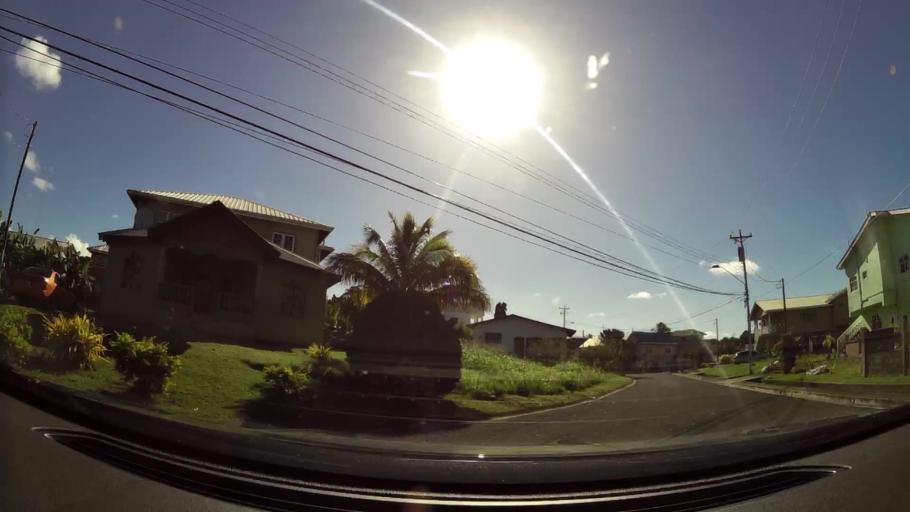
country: TT
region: Tobago
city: Scarborough
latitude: 11.1596
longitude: -60.8273
